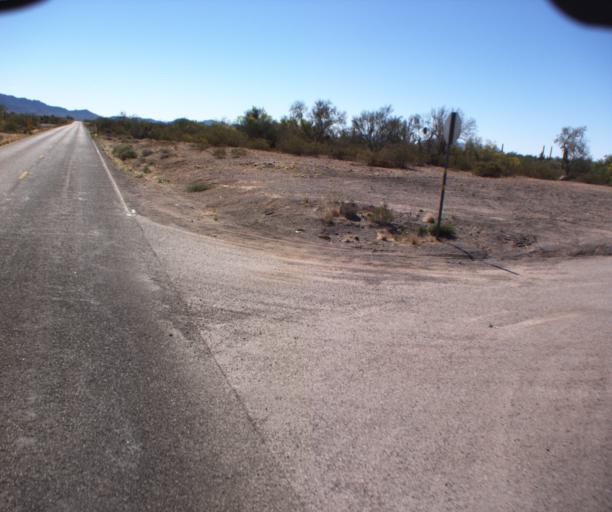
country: US
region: Arizona
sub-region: Pima County
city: Ajo
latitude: 32.3560
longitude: -112.8270
